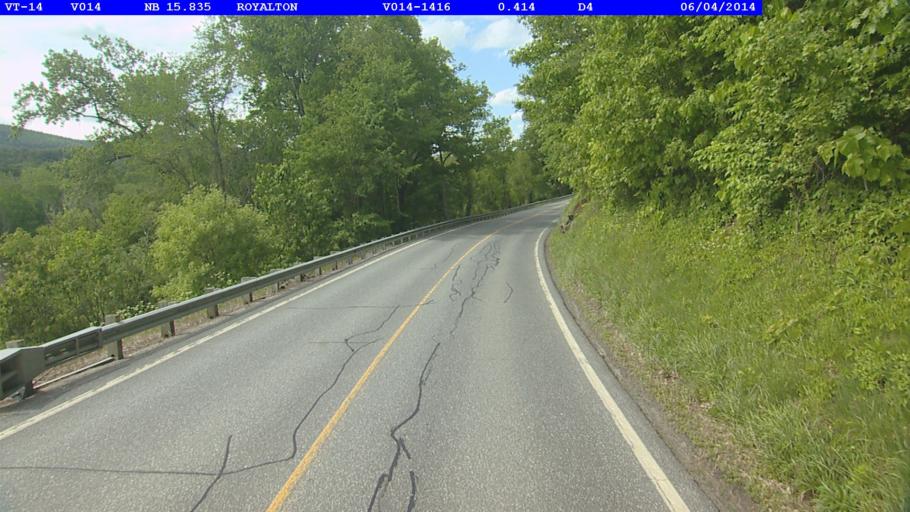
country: US
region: Vermont
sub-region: Windsor County
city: Woodstock
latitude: 43.8005
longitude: -72.5008
